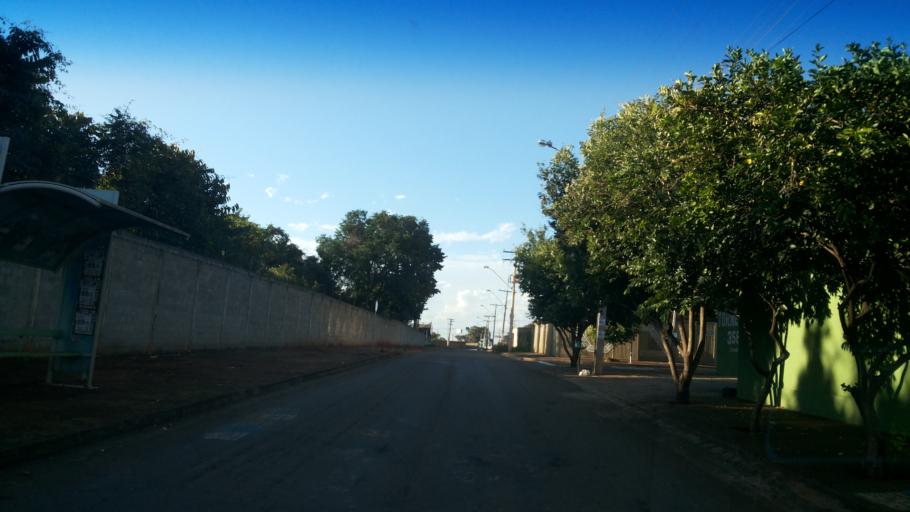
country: BR
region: Goias
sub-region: Goiania
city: Goiania
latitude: -16.6446
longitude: -49.3013
